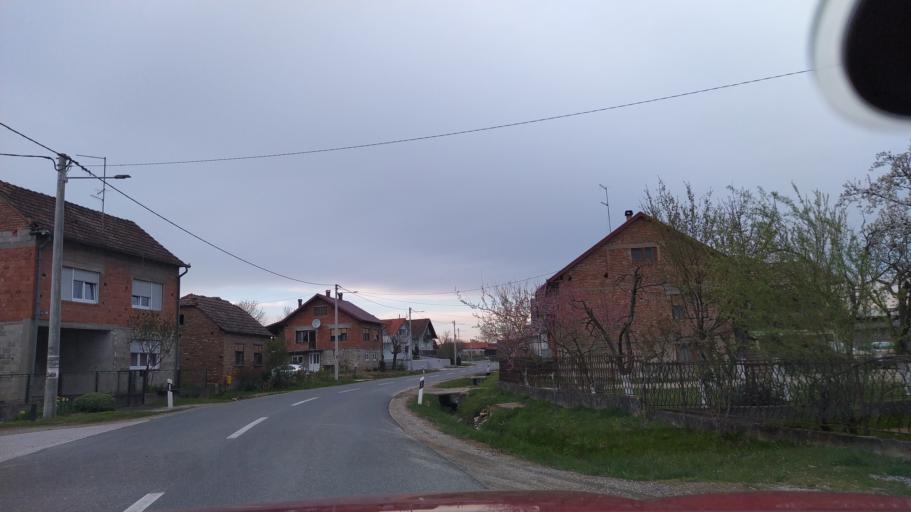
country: HR
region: Varazdinska
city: Ludbreg
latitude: 46.2348
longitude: 16.5474
